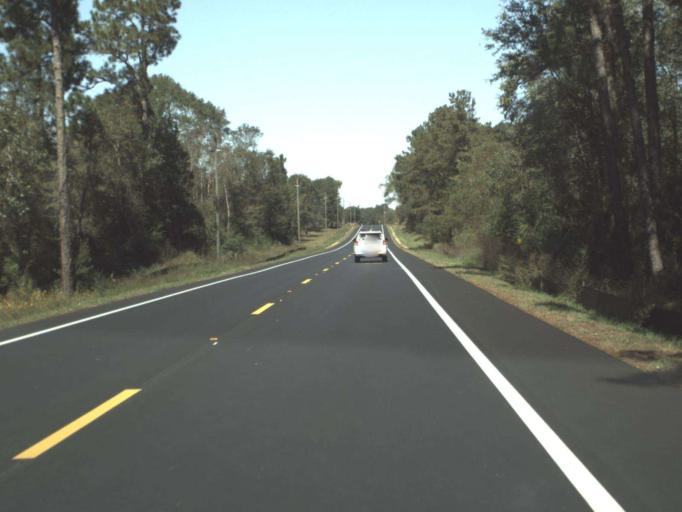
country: US
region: Alabama
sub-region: Covington County
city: Florala
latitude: 30.9378
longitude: -86.2820
